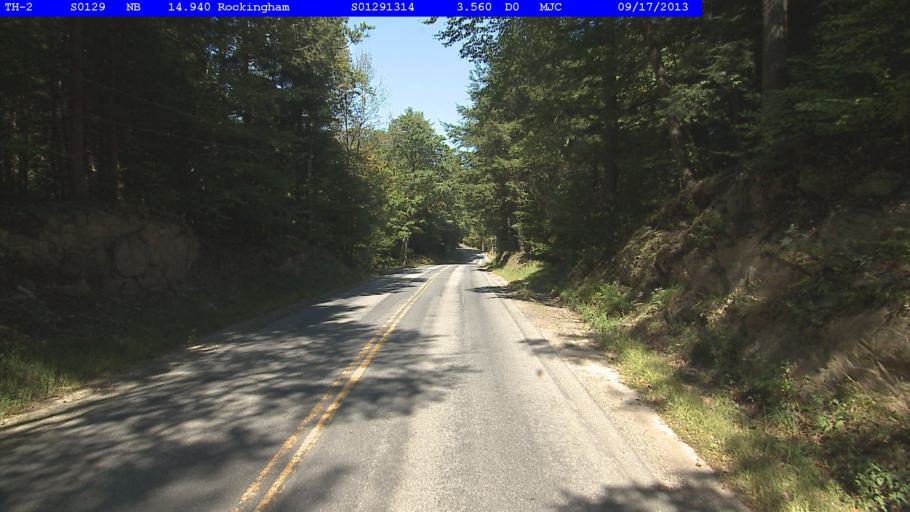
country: US
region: Vermont
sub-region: Windham County
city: Rockingham
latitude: 43.1685
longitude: -72.5176
